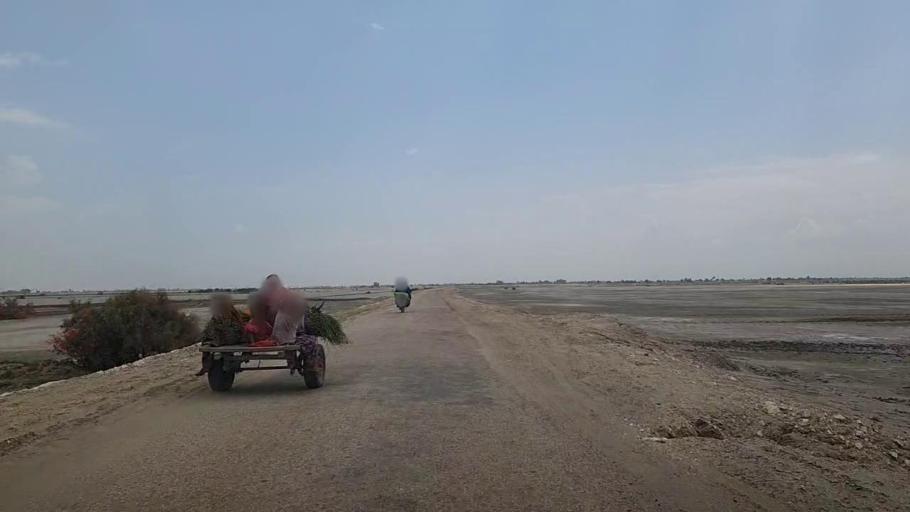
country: PK
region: Sindh
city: Kandhkot
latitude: 28.2870
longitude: 69.1523
